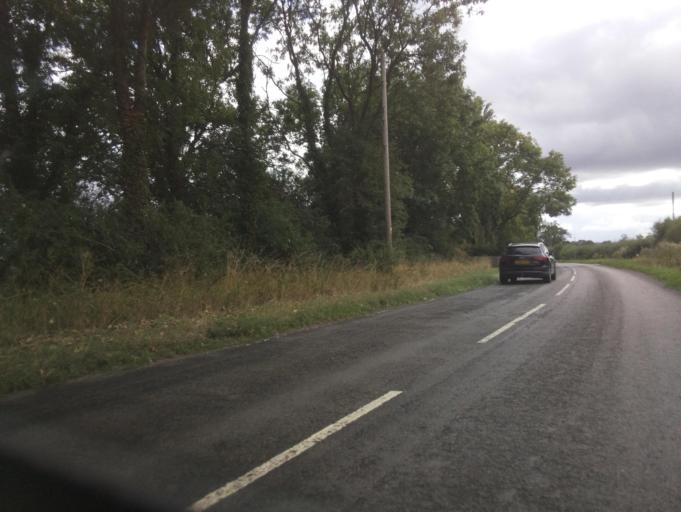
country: GB
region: England
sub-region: Leicestershire
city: Loughborough
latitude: 52.7995
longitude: -1.1955
